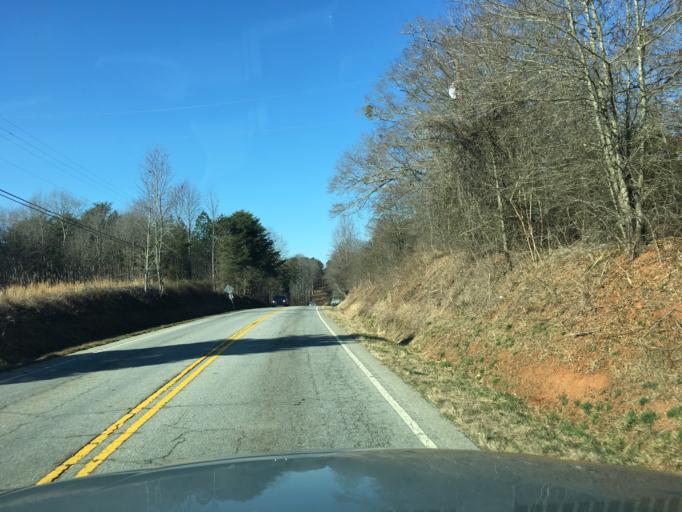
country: US
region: South Carolina
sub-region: Greenville County
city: Berea
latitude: 34.8869
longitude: -82.5146
